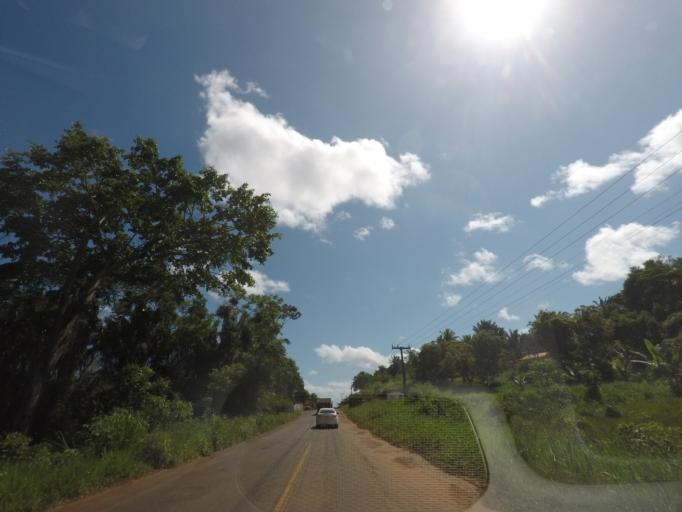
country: BR
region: Bahia
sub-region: Itubera
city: Itubera
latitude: -13.6716
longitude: -39.1225
